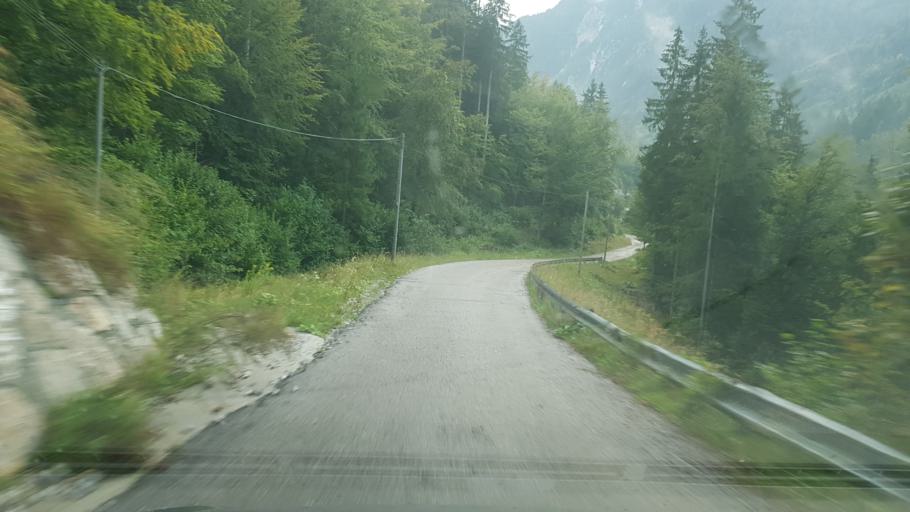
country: IT
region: Friuli Venezia Giulia
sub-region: Provincia di Udine
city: Tarvisio
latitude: 46.4859
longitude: 13.6148
